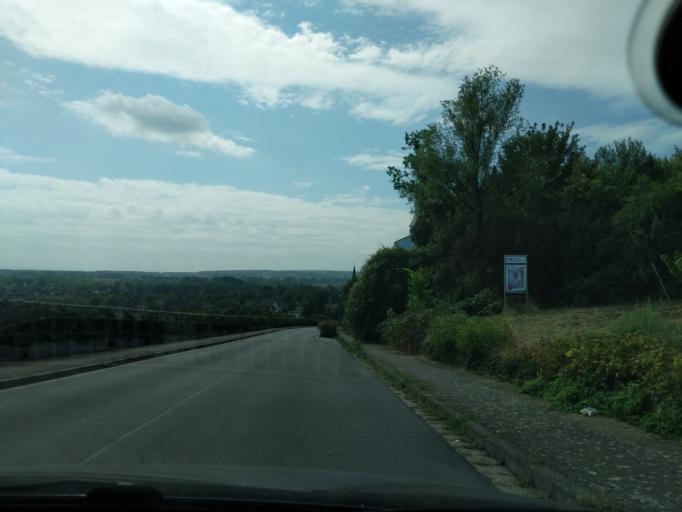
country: DE
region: Rheinland-Pfalz
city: Bodenheim
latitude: 49.9668
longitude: 8.3100
